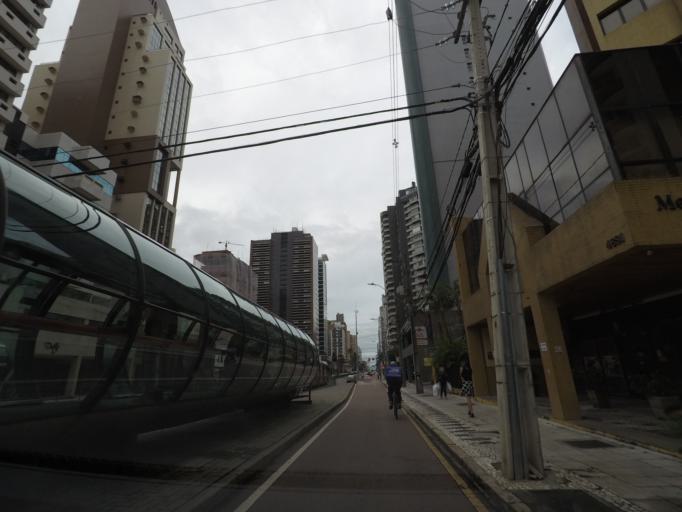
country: BR
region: Parana
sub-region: Curitiba
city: Curitiba
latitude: -25.4449
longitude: -49.2855
